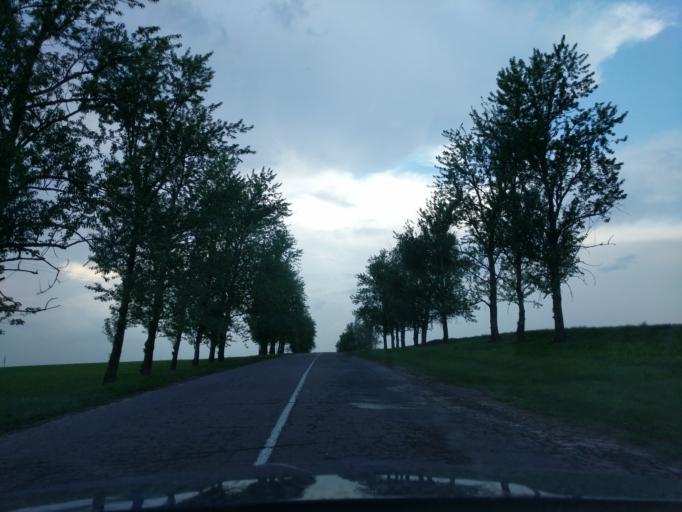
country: BY
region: Minsk
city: Novy Svyerzhan'
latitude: 53.4758
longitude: 26.6325
